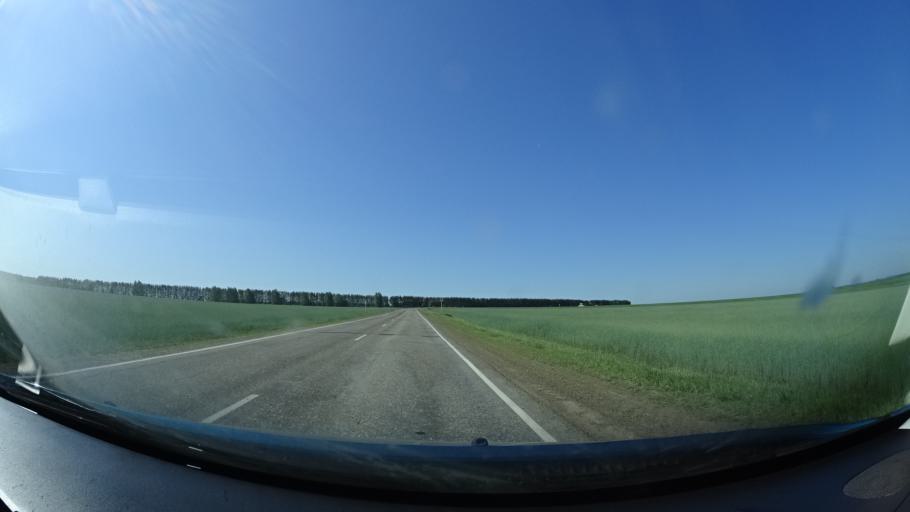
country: RU
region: Bashkortostan
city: Starobaltachevo
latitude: 55.9383
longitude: 55.8288
